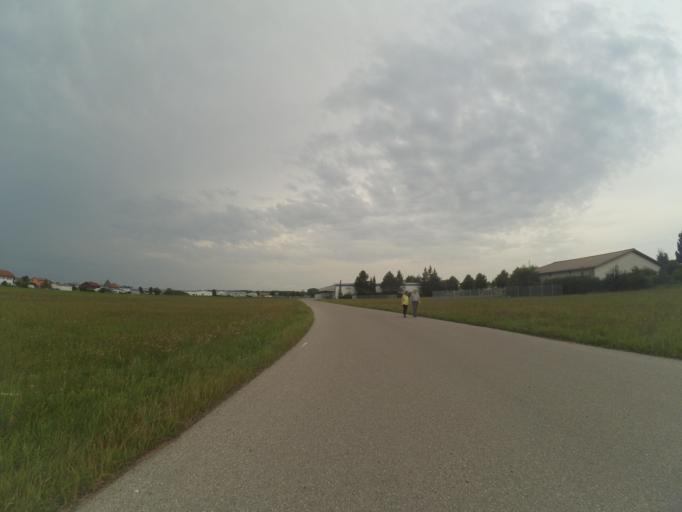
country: DE
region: Bavaria
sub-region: Swabia
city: Buchloe
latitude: 48.0395
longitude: 10.7160
